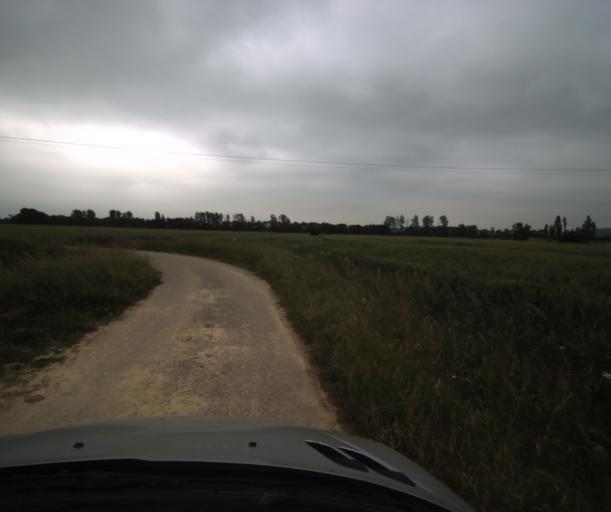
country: FR
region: Midi-Pyrenees
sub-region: Departement du Tarn-et-Garonne
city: Saint-Nicolas-de-la-Grave
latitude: 44.0534
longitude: 0.9801
